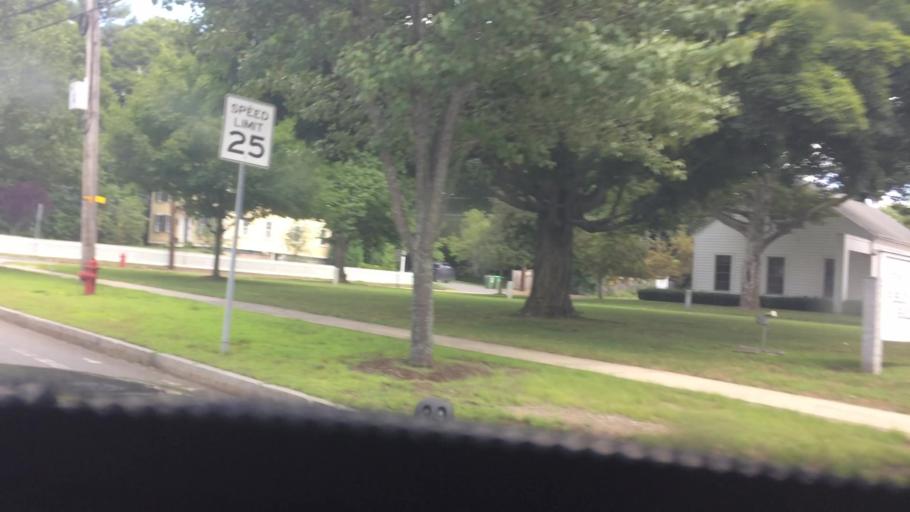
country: US
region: Massachusetts
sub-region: Middlesex County
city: Wayland
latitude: 42.3631
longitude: -71.3602
